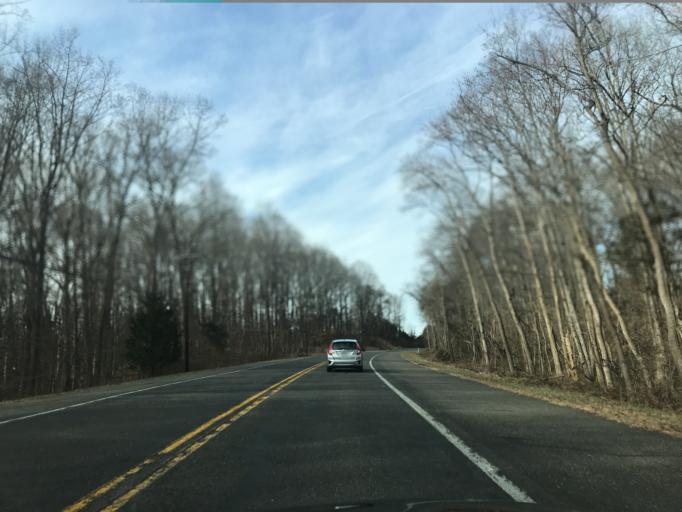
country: US
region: Maryland
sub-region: Charles County
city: La Plata
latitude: 38.4807
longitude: -77.0896
